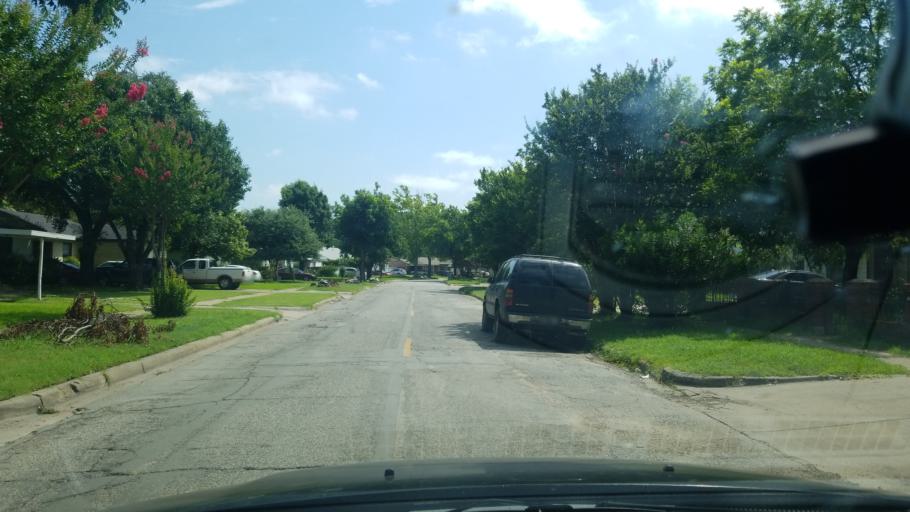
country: US
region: Texas
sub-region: Dallas County
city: Balch Springs
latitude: 32.7382
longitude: -96.6895
